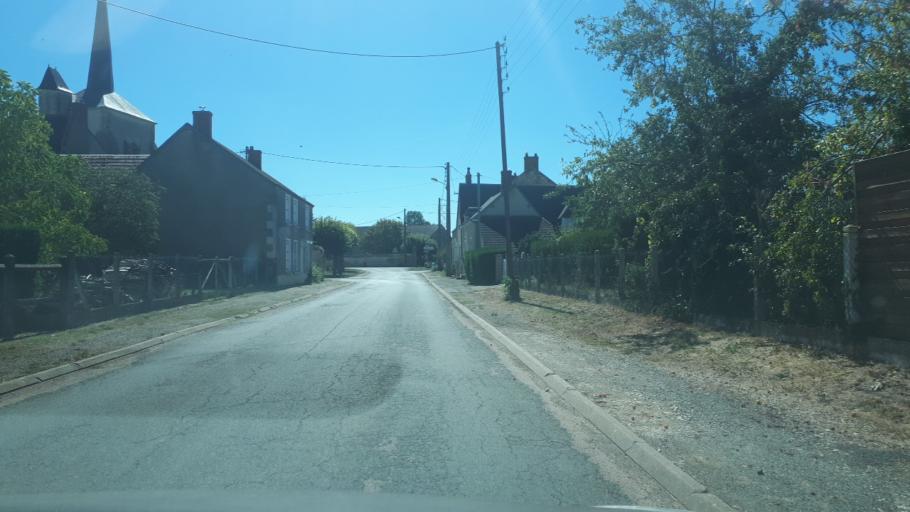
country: FR
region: Centre
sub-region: Departement du Cher
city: Rians
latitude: 47.1846
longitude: 2.7075
